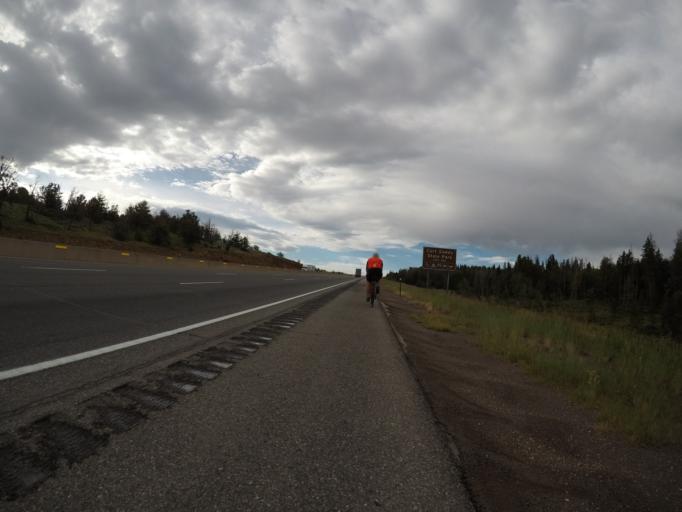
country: US
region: Wyoming
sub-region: Albany County
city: Laramie
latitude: 41.2504
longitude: -105.4446
